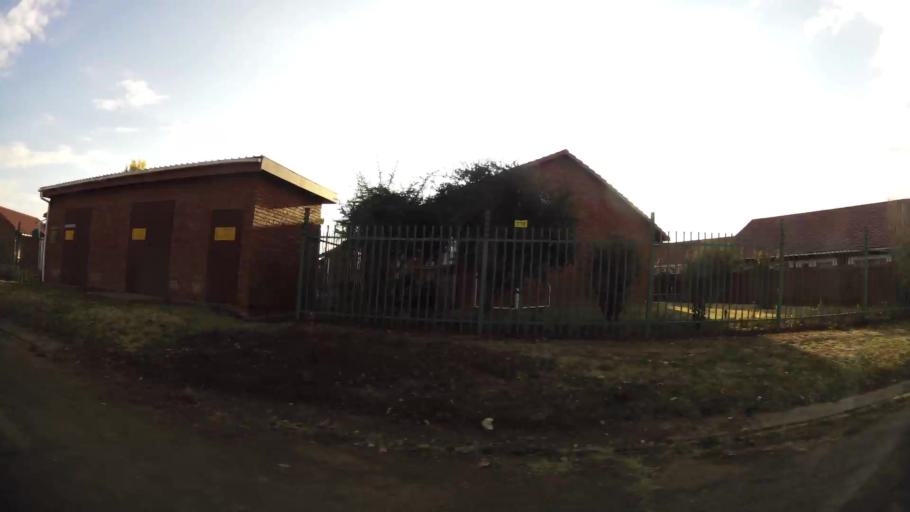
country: ZA
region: Orange Free State
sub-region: Mangaung Metropolitan Municipality
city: Bloemfontein
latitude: -29.1498
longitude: 26.1891
